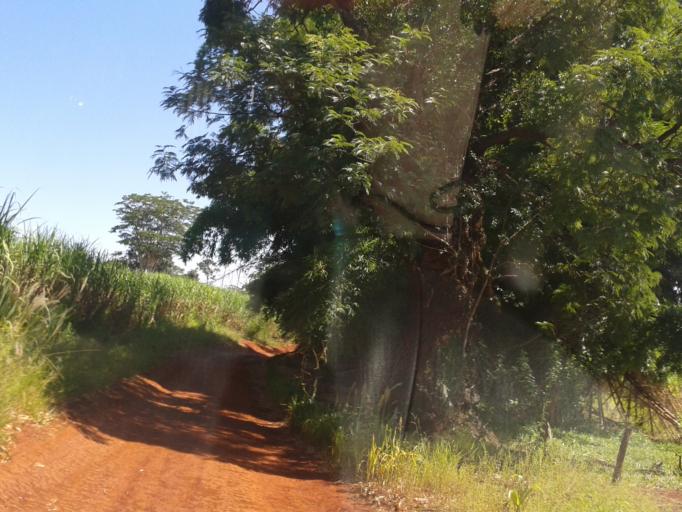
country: BR
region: Minas Gerais
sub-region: Centralina
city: Centralina
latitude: -18.6349
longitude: -49.2984
